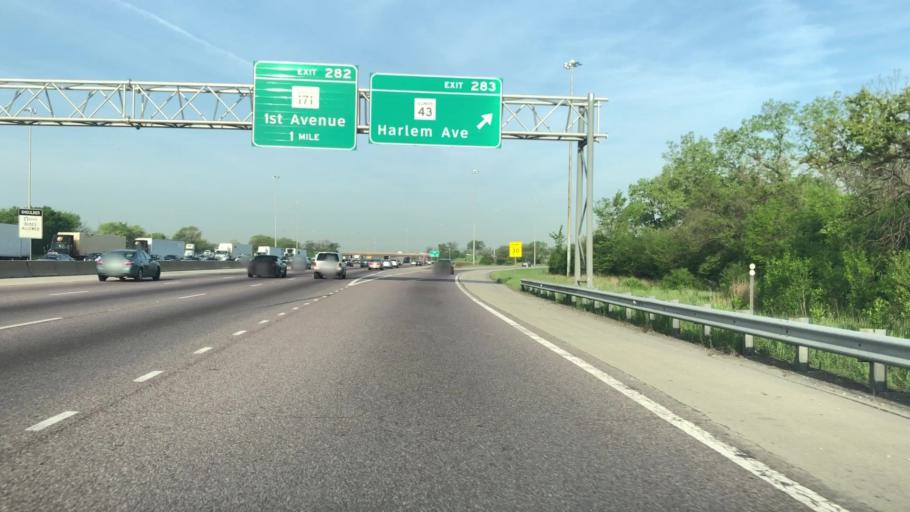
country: US
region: Illinois
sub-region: Cook County
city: Summit
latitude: 41.8010
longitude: -87.7952
